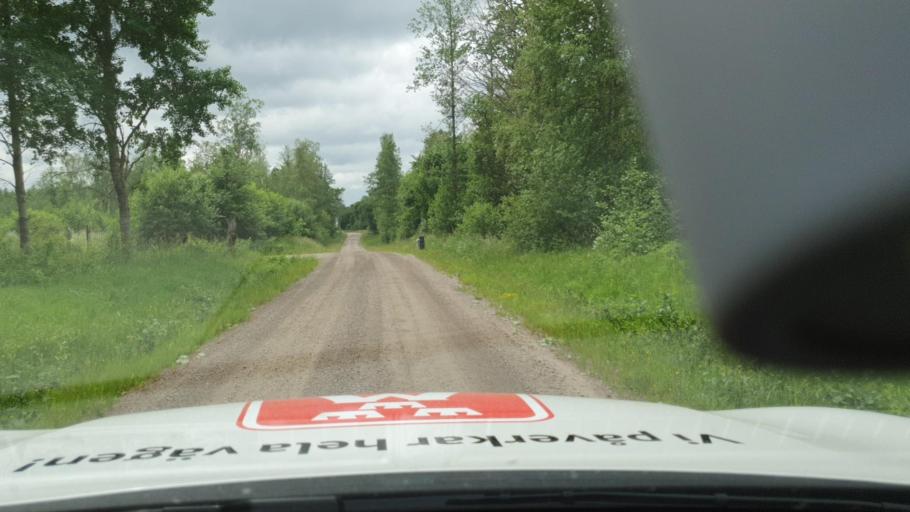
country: SE
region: Vaestra Goetaland
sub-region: Tidaholms Kommun
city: Olofstorp
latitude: 58.1723
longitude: 14.0944
